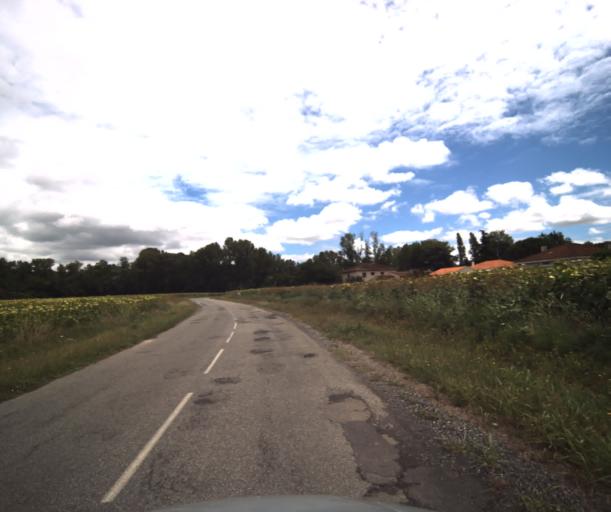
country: FR
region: Midi-Pyrenees
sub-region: Departement de la Haute-Garonne
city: Lacroix-Falgarde
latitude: 43.4809
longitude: 1.4069
